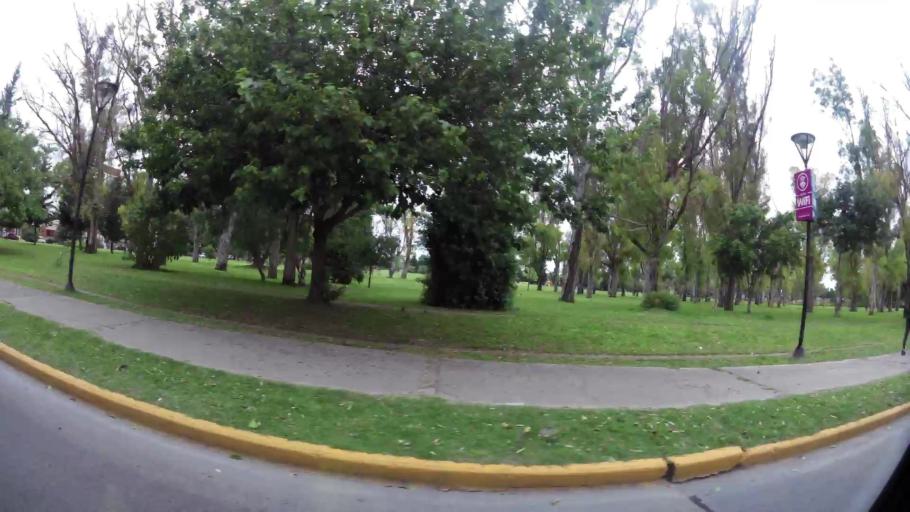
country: AR
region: Buenos Aires
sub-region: Partido de La Plata
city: La Plata
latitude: -34.9212
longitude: -57.9812
